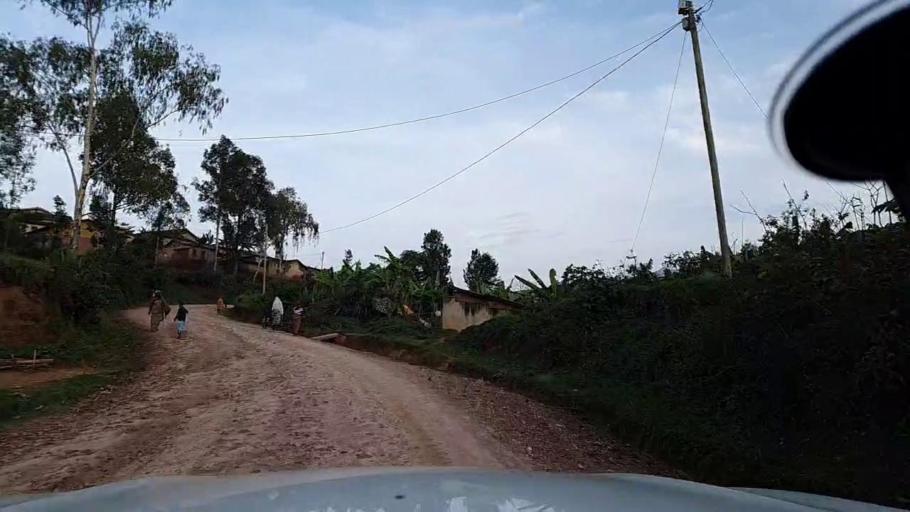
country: RW
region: Southern Province
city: Nyanza
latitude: -2.2110
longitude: 29.6083
